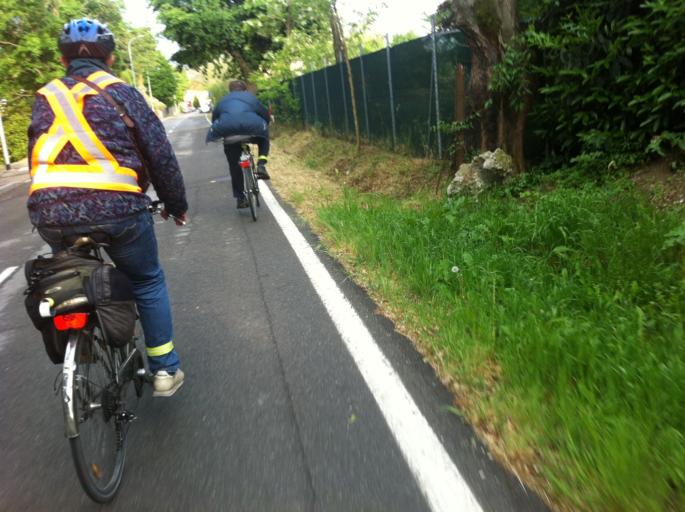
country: IT
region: Emilia-Romagna
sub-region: Provincia di Bologna
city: San Lazzaro
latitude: 44.4908
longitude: 11.3896
